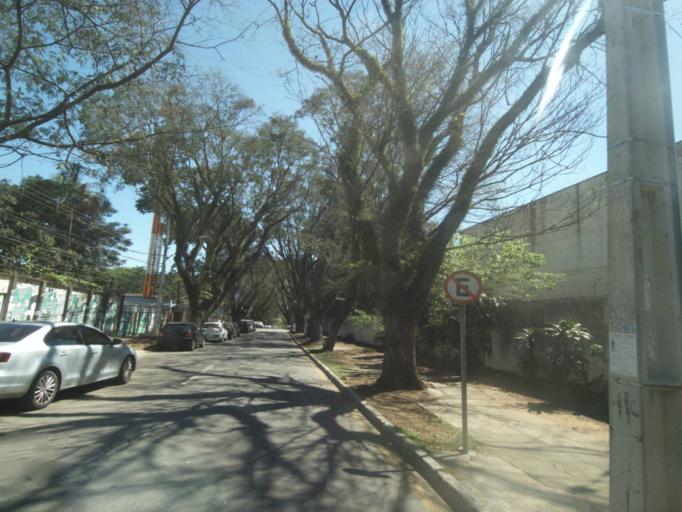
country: BR
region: Parana
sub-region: Curitiba
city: Curitiba
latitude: -25.4016
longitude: -49.2443
